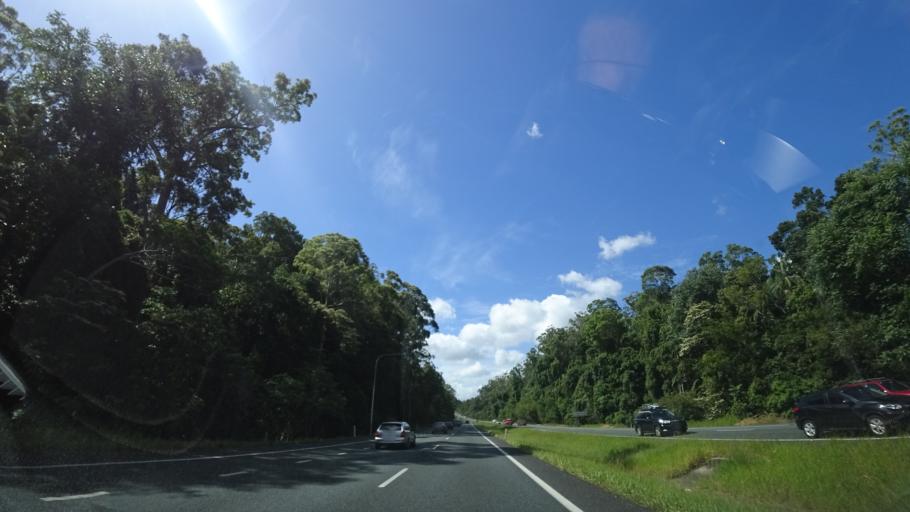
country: AU
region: Queensland
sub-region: Sunshine Coast
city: Woombye
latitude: -26.6688
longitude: 152.9973
